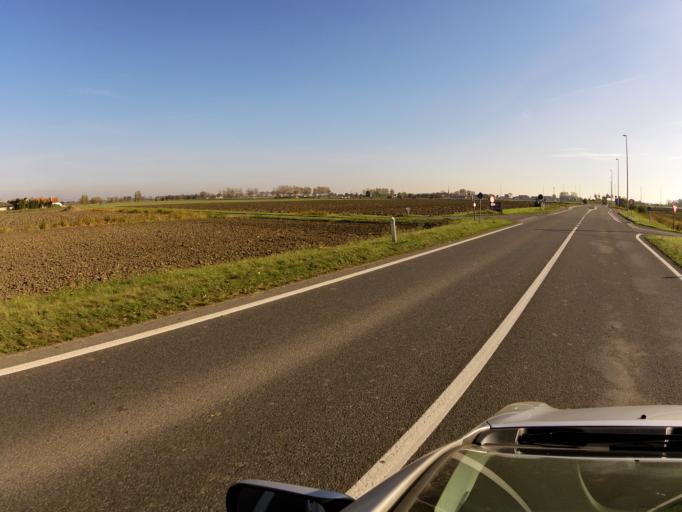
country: BE
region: Flanders
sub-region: Provincie West-Vlaanderen
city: Veurne
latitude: 51.0743
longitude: 2.7187
